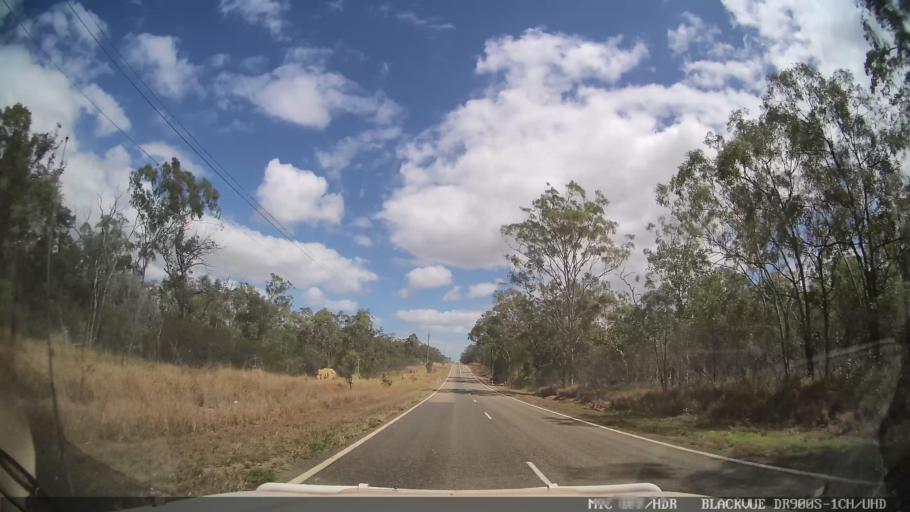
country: AU
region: Queensland
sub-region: Tablelands
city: Ravenshoe
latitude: -17.7233
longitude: 145.0516
